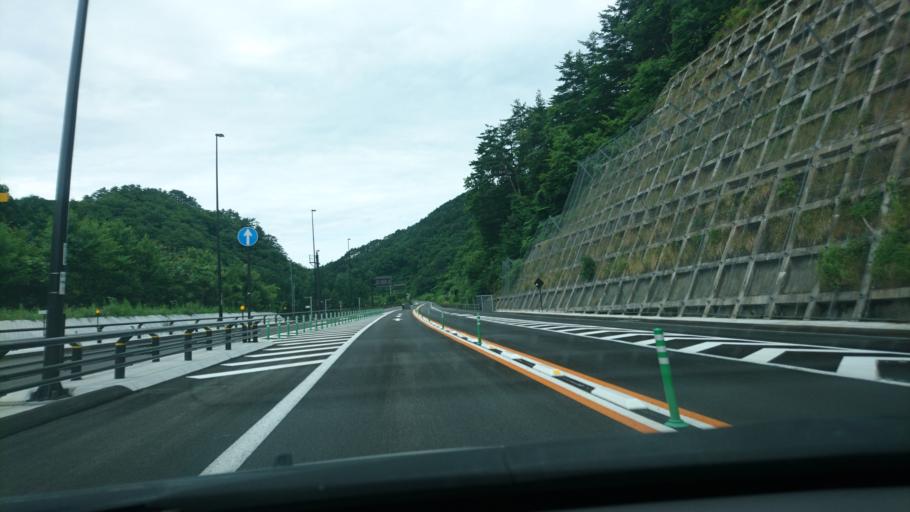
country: JP
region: Iwate
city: Miyako
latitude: 39.8435
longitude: 141.9536
